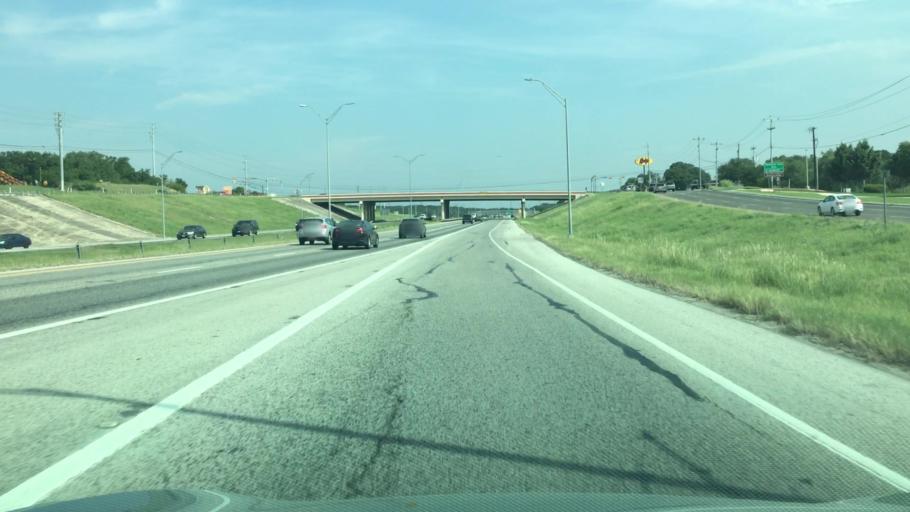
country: US
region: Texas
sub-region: Bexar County
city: Leon Valley
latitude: 29.4606
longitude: -98.6903
